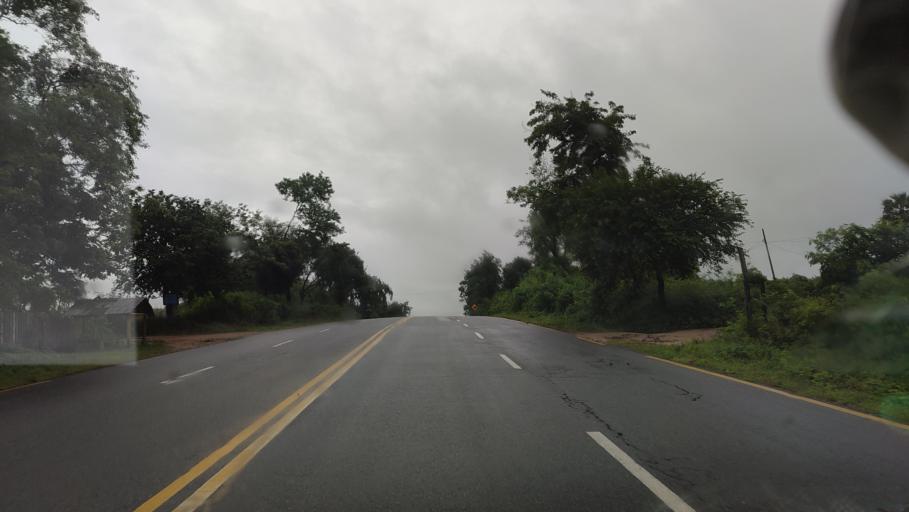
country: MM
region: Mandalay
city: Pyinmana
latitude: 19.9468
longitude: 96.2533
